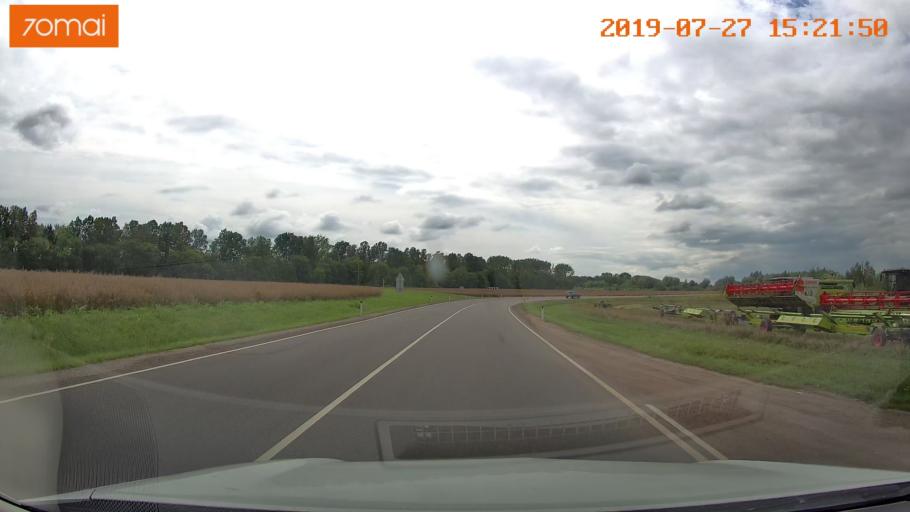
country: LT
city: Kybartai
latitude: 54.6330
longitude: 22.6714
